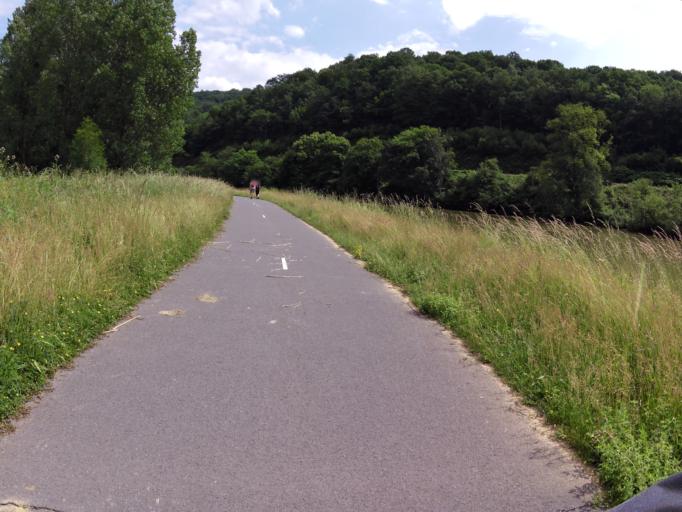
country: FR
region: Champagne-Ardenne
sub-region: Departement des Ardennes
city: Nouzonville
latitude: 49.8323
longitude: 4.7719
